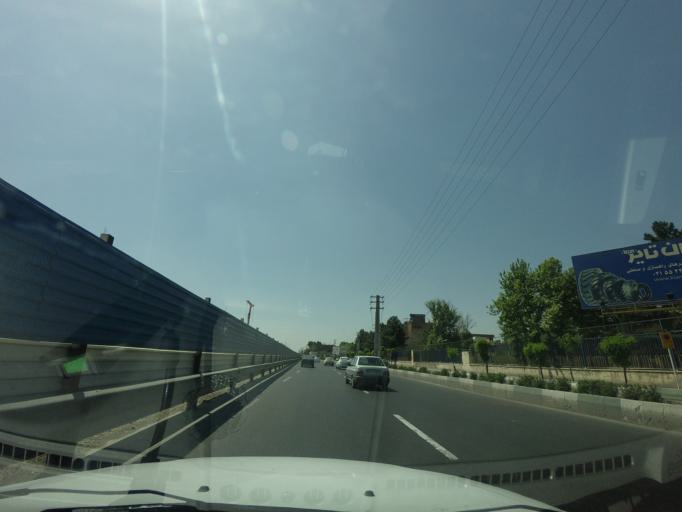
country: IR
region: Tehran
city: Eslamshahr
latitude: 35.6055
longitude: 51.3045
